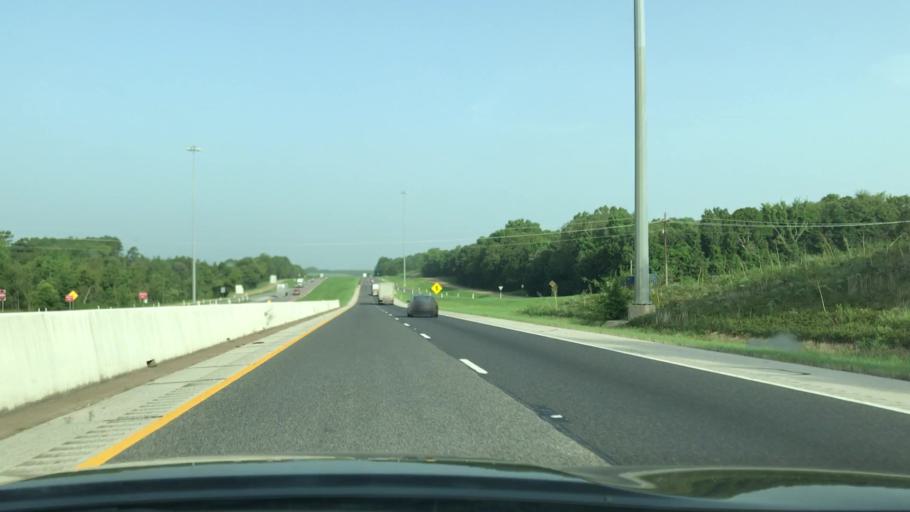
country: US
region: Texas
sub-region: Smith County
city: Tyler
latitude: 32.4534
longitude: -95.2847
